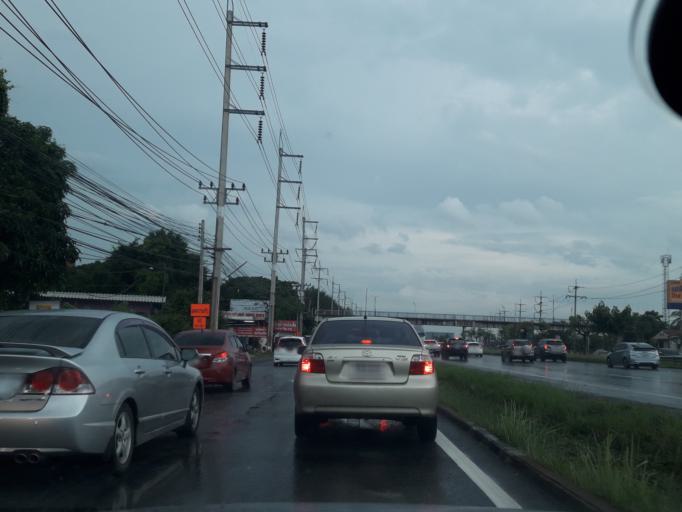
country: TH
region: Sara Buri
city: Nong Khae
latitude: 14.3839
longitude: 100.8866
